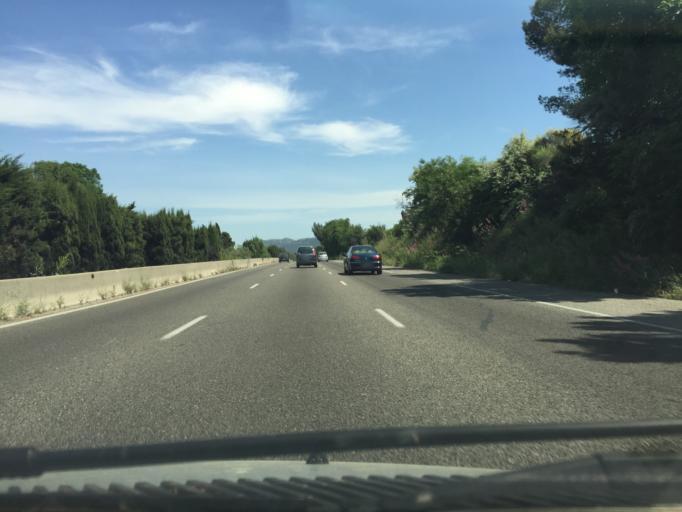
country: FR
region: Provence-Alpes-Cote d'Azur
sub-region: Departement des Bouches-du-Rhone
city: La Penne-sur-Huveaune
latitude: 43.2906
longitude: 5.4879
